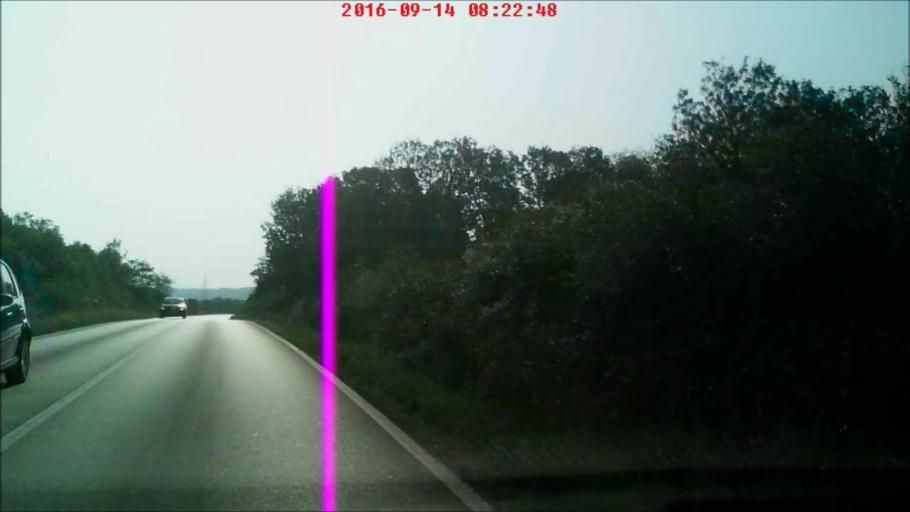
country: HR
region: Zadarska
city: Nin
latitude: 44.2160
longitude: 15.2226
